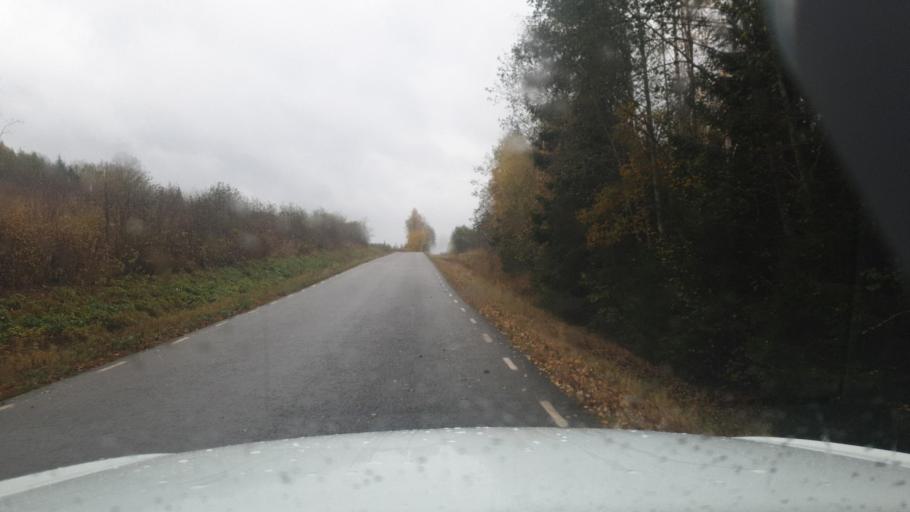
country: SE
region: Vaermland
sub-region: Torsby Kommun
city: Torsby
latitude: 60.0129
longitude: 12.6671
